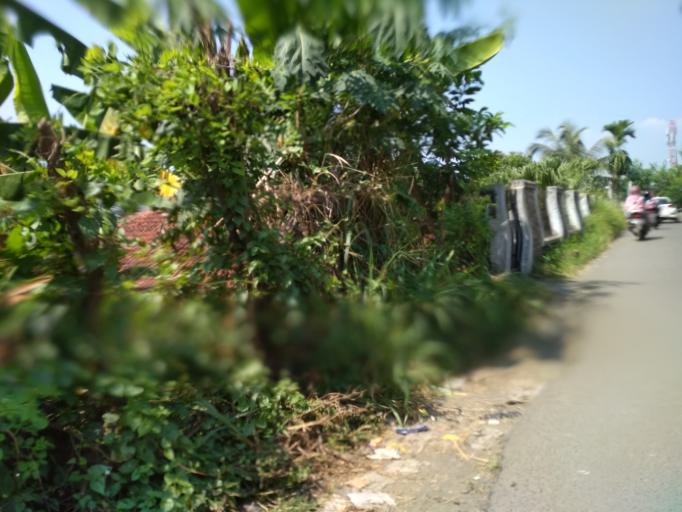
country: ID
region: West Java
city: Ciampea
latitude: -6.5598
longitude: 106.7439
